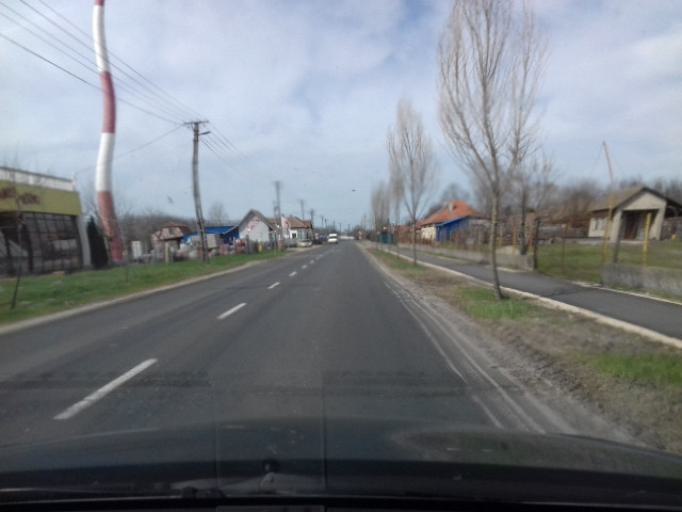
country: HU
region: Jasz-Nagykun-Szolnok
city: Cserkeszolo
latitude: 46.8639
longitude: 20.2002
